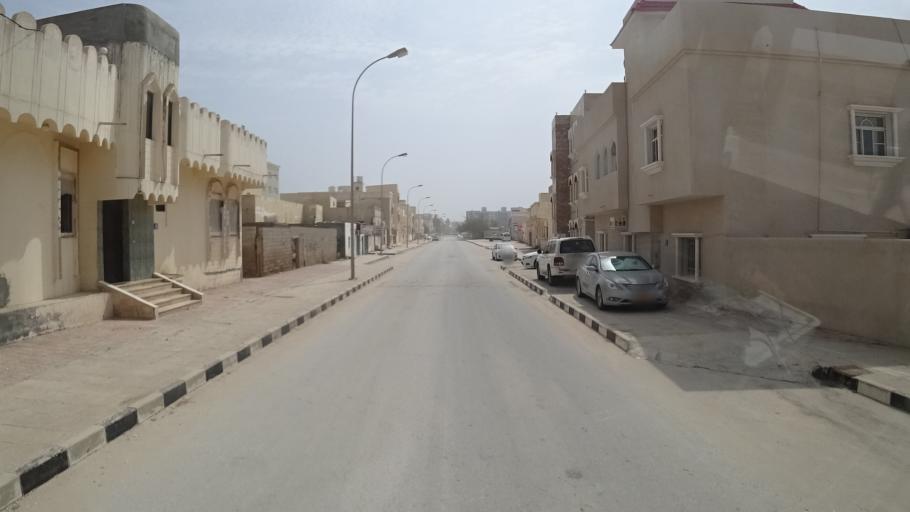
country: OM
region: Zufar
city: Salalah
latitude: 17.0099
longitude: 54.1611
